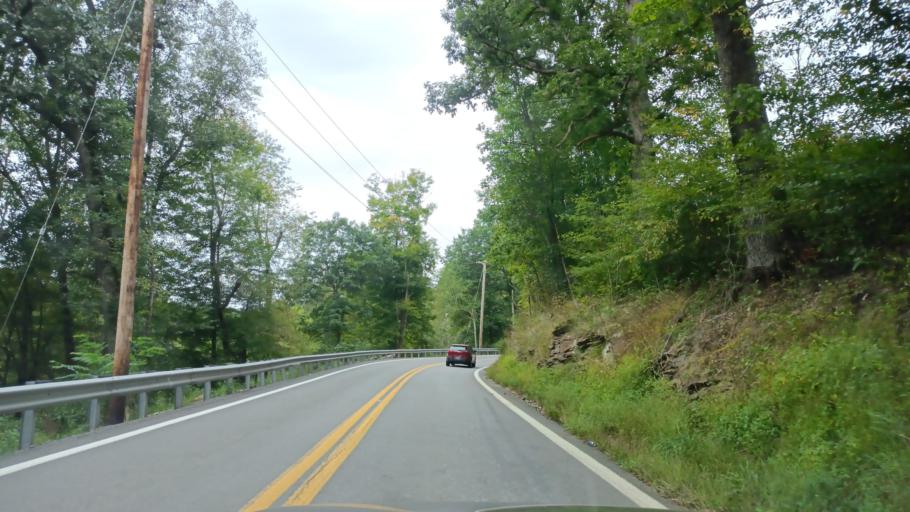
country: US
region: West Virginia
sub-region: Taylor County
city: Grafton
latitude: 39.3300
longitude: -79.9162
